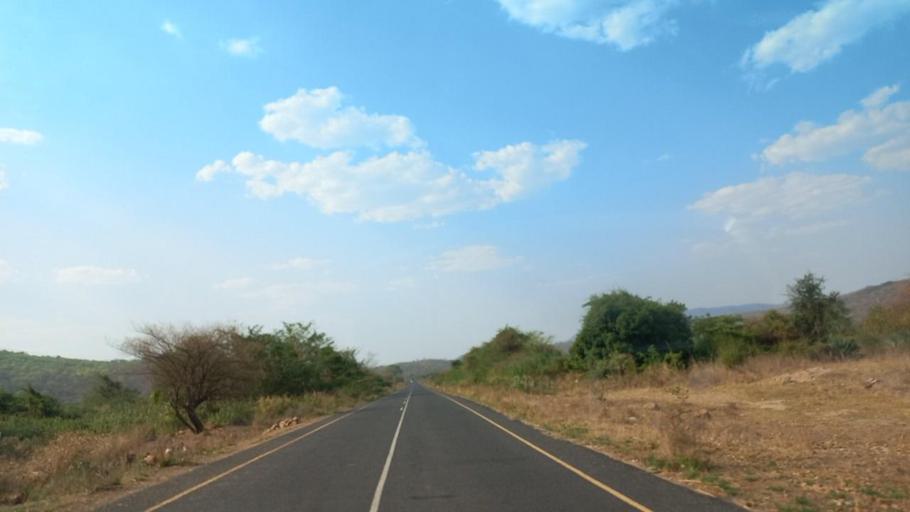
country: ZM
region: Lusaka
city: Luangwa
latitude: -15.0259
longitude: 30.2251
